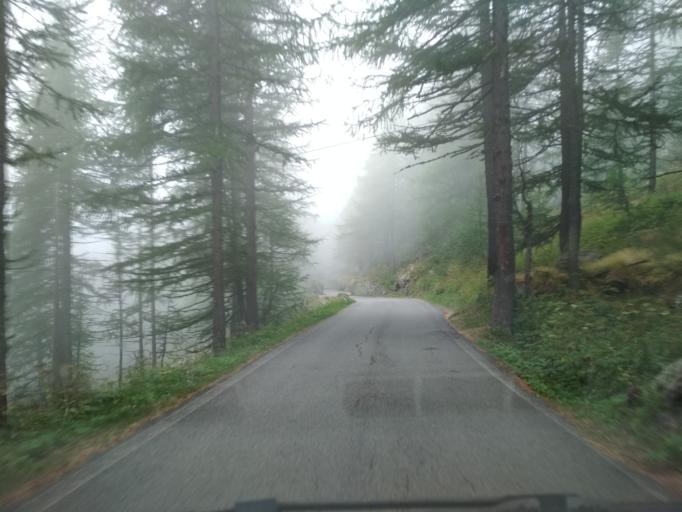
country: IT
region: Piedmont
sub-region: Provincia di Torino
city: Balme
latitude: 45.3029
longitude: 7.1967
